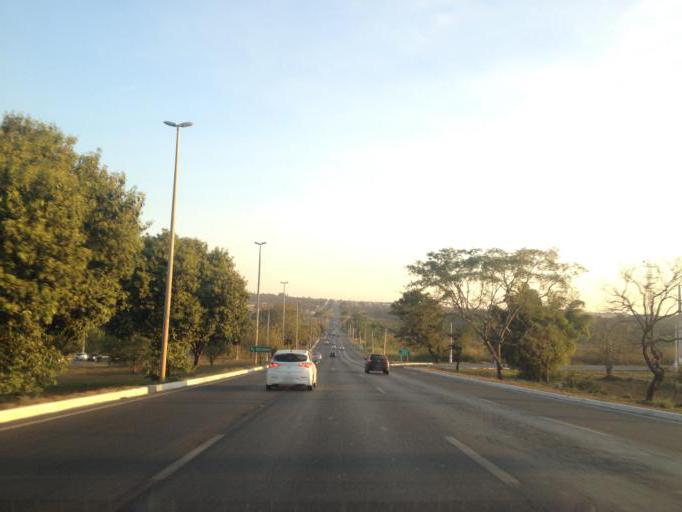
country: BR
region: Federal District
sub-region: Brasilia
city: Brasilia
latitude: -15.7238
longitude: -47.9070
